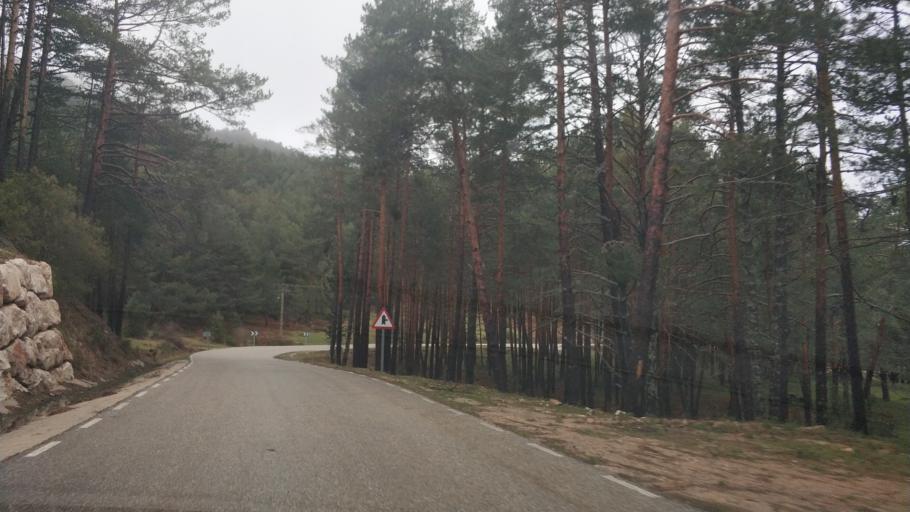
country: ES
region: Castille and Leon
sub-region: Provincia de Burgos
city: Neila
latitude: 42.0235
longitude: -3.0136
